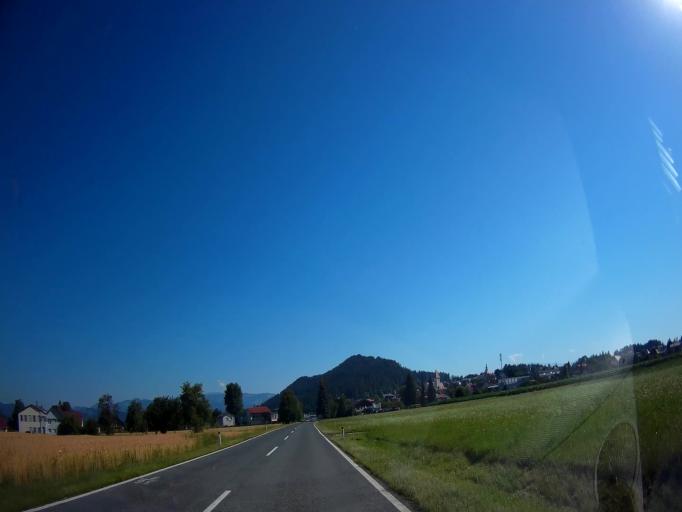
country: AT
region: Carinthia
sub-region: Politischer Bezirk Volkermarkt
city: Eberndorf
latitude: 46.5859
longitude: 14.6346
